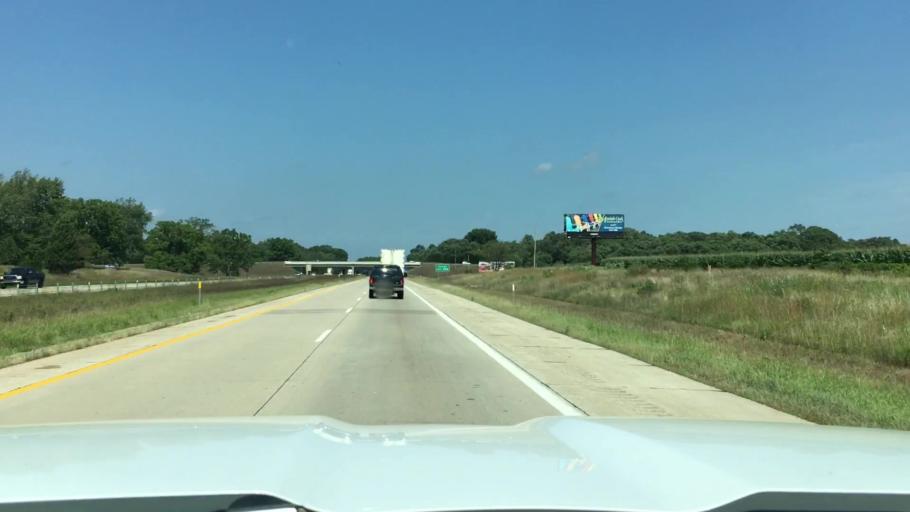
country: US
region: Michigan
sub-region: Allegan County
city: Plainwell
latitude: 42.4316
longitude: -85.6606
